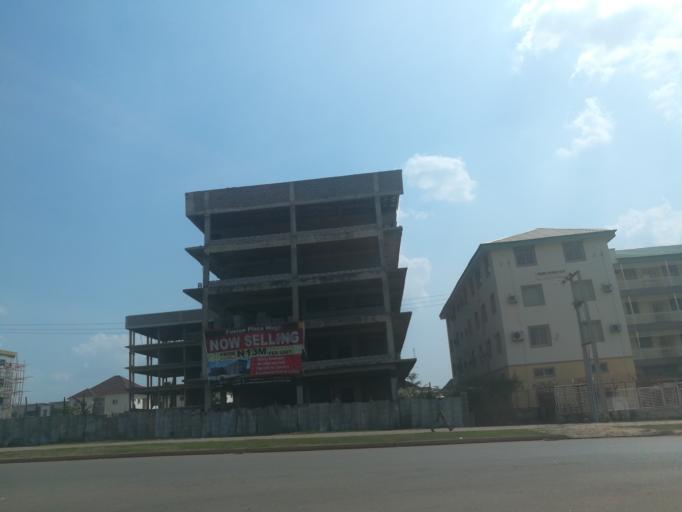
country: NG
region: Abuja Federal Capital Territory
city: Abuja
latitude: 9.0546
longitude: 7.4385
